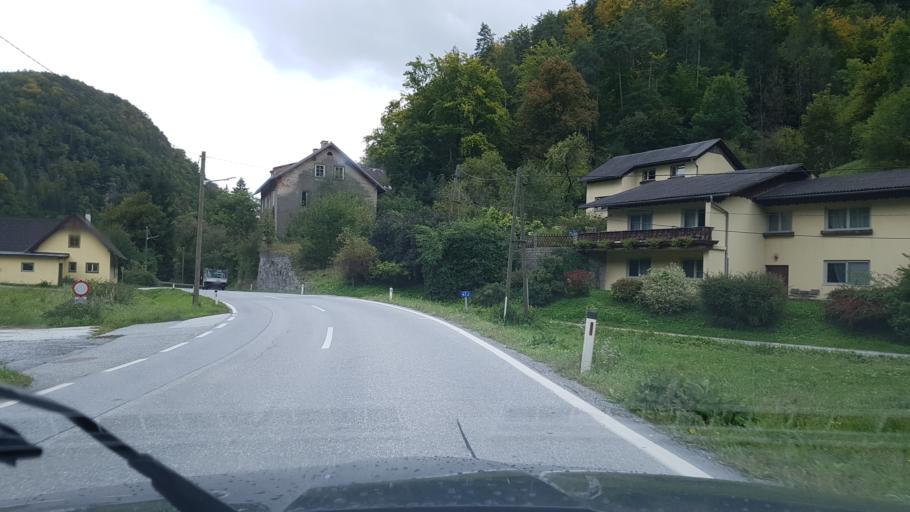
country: AT
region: Styria
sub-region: Politischer Bezirk Voitsberg
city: Piberegg
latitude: 47.0808
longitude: 15.0691
